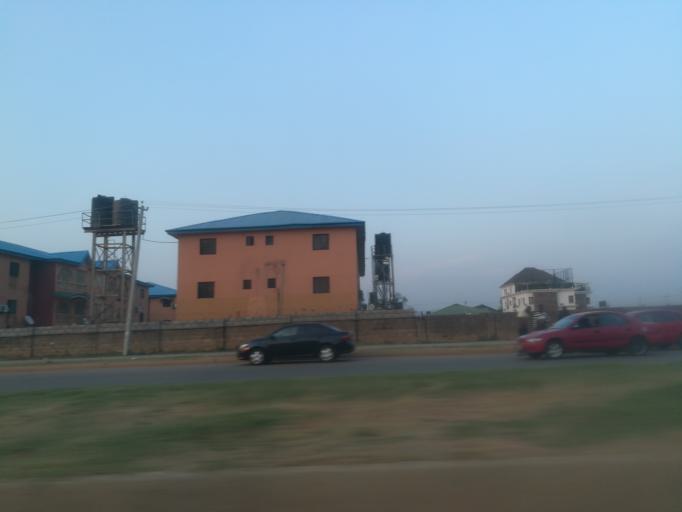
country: NG
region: Abuja Federal Capital Territory
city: Abuja
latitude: 9.0543
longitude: 7.4415
